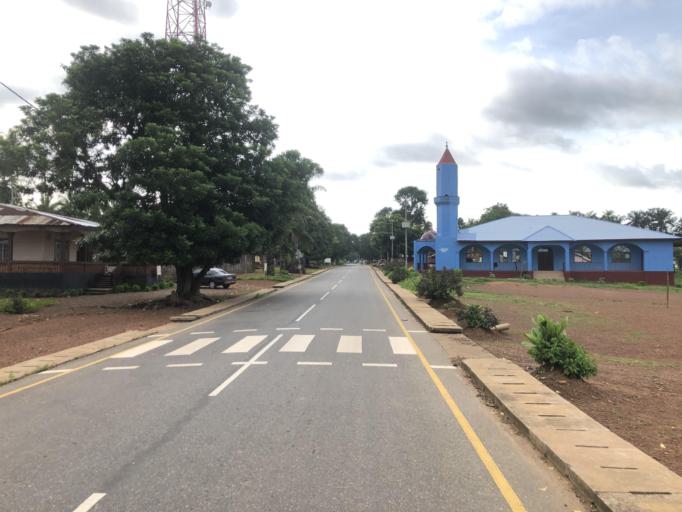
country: SL
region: Northern Province
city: Port Loko
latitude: 8.7698
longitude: -12.7906
